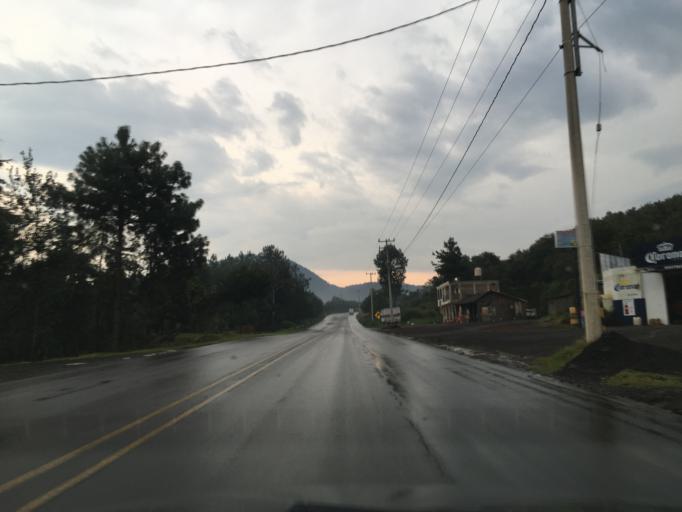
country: MX
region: Michoacan
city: Capacuaro
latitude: 19.5289
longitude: -102.0988
